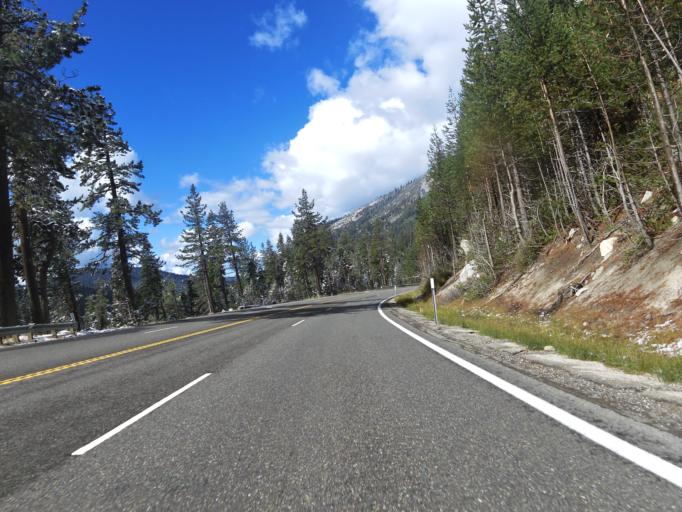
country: US
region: California
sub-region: El Dorado County
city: South Lake Tahoe
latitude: 38.8225
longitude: -120.0643
